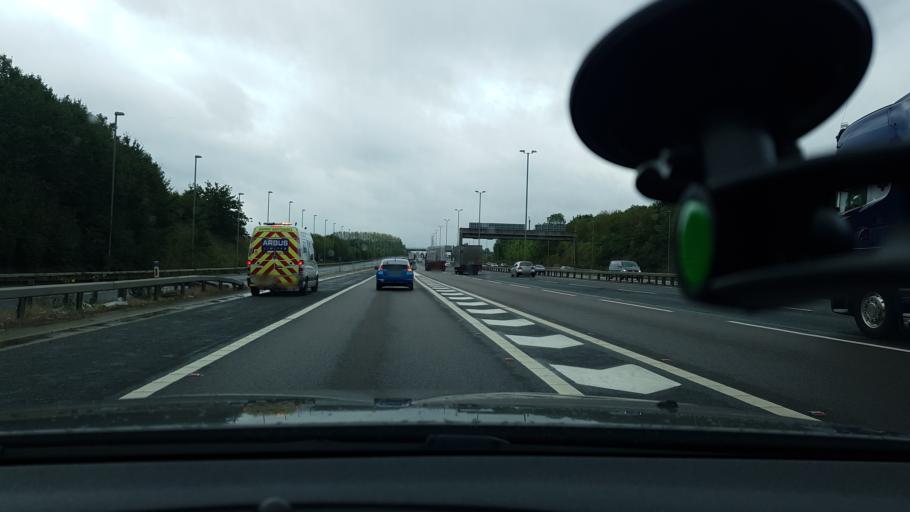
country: GB
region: England
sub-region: Essex
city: Stansted
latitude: 51.8679
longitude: 0.1967
